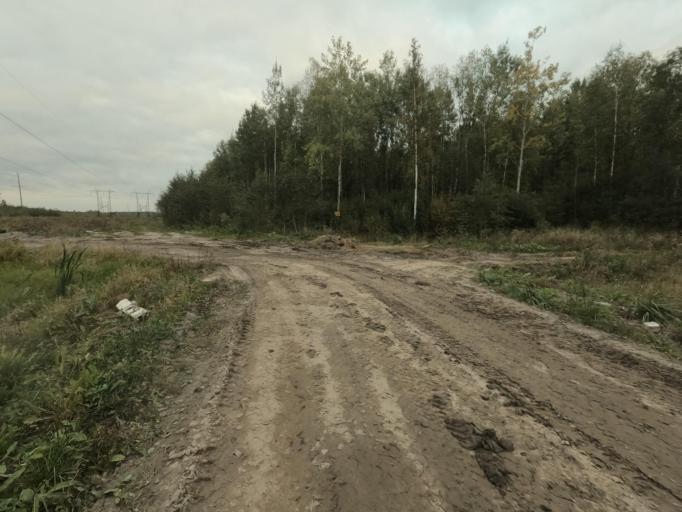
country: RU
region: St.-Petersburg
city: Sapernyy
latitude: 59.7537
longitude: 30.7013
